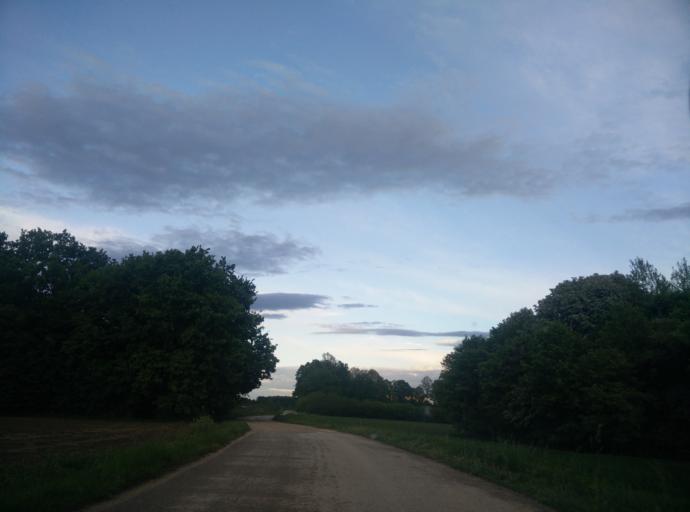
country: BA
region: Brcko
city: Brcko
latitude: 44.7835
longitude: 18.8186
